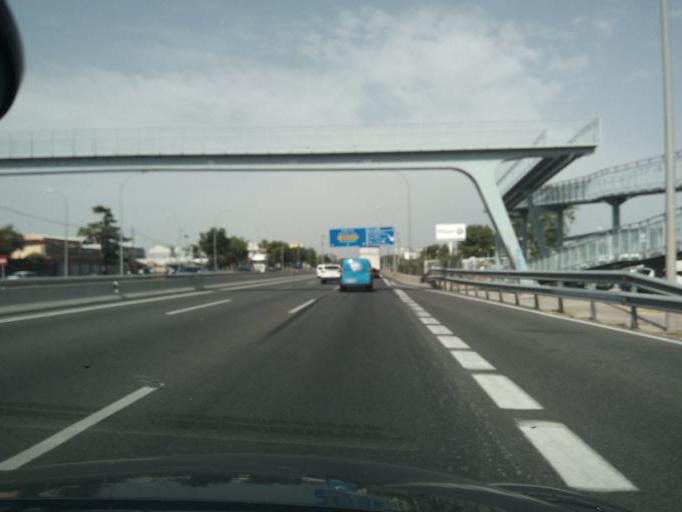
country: ES
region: Madrid
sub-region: Provincia de Madrid
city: Coslada
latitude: 40.4498
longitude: -3.5658
